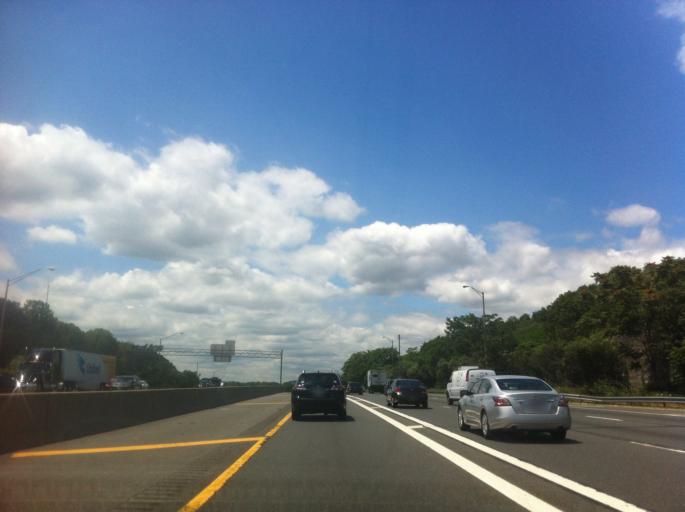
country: US
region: New York
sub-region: Suffolk County
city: Dix Hills
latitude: 40.8016
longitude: -73.3319
